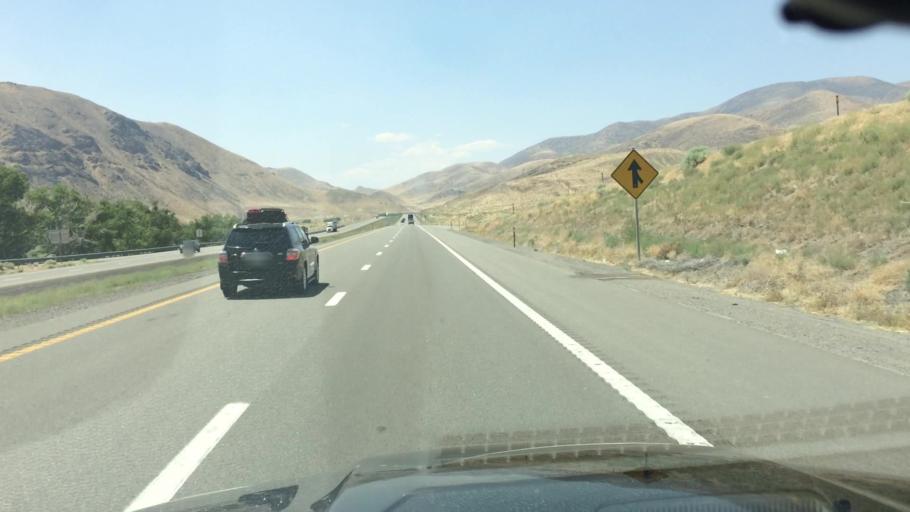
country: US
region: Nevada
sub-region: Lyon County
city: Fernley
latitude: 39.5895
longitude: -119.4296
